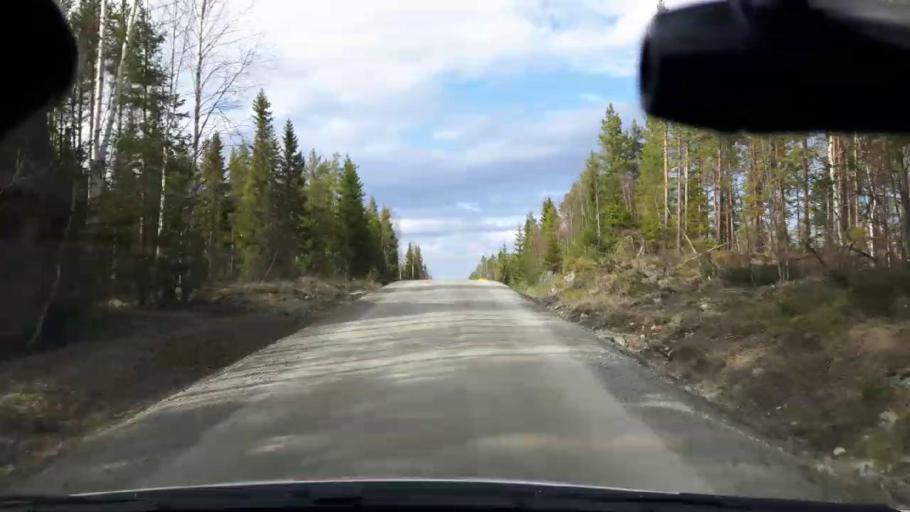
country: SE
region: Jaemtland
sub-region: Bergs Kommun
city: Hoverberg
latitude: 62.9104
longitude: 14.6346
